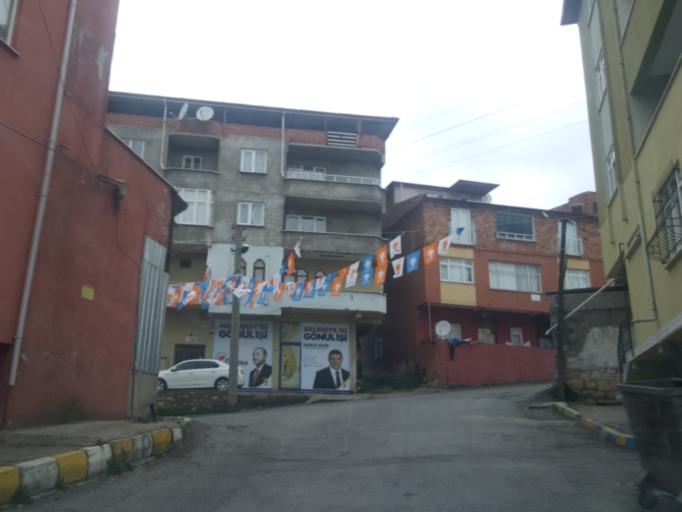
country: TR
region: Kocaeli
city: Tavsancil
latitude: 40.7863
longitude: 29.5431
